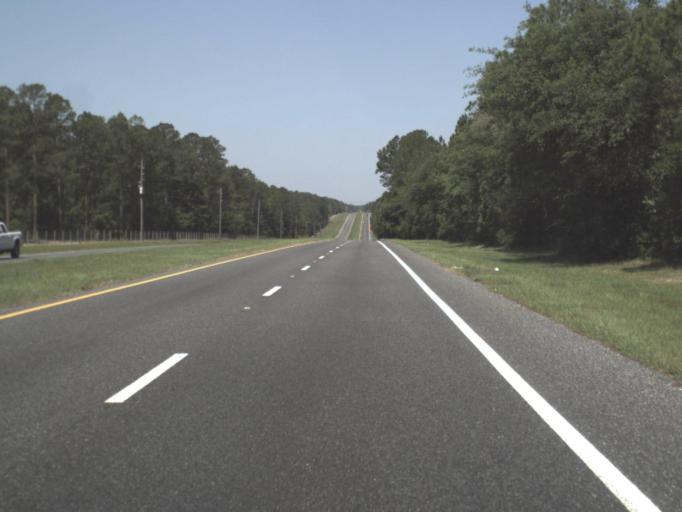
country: US
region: Florida
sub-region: Clay County
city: Middleburg
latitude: 29.9820
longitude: -81.9407
